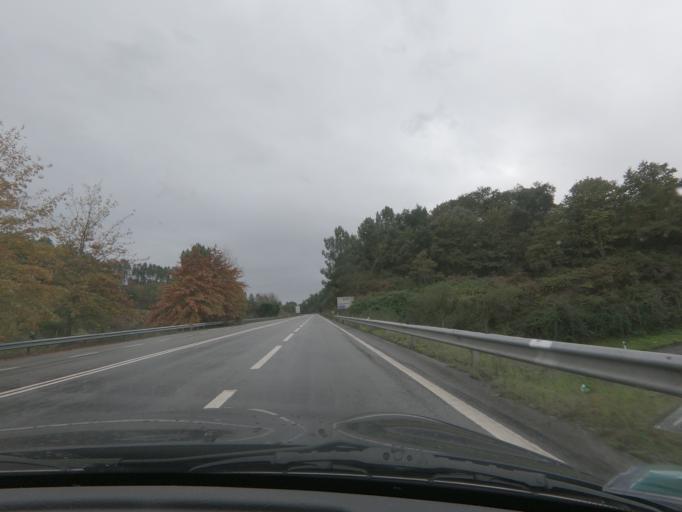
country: PT
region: Porto
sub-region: Amarante
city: Teloes
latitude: 41.3126
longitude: -8.0748
